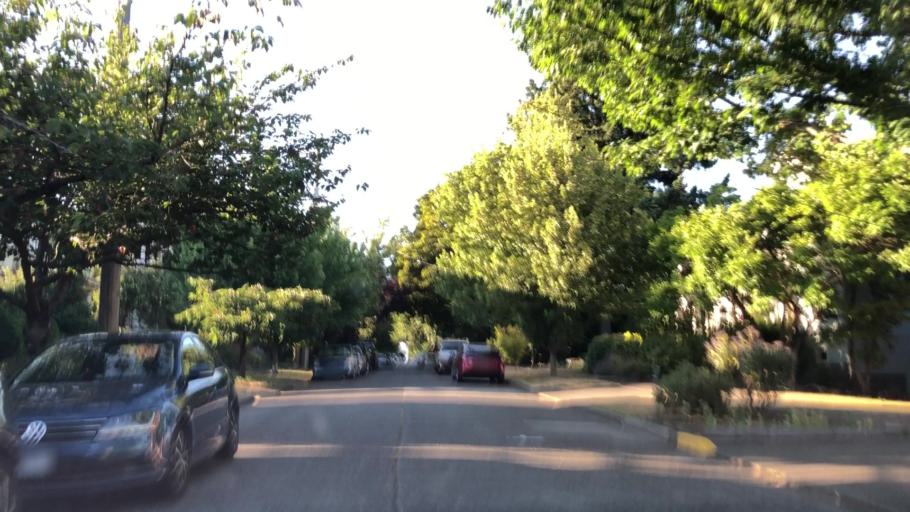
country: US
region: Washington
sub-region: King County
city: Seattle
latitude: 47.6524
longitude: -122.3351
